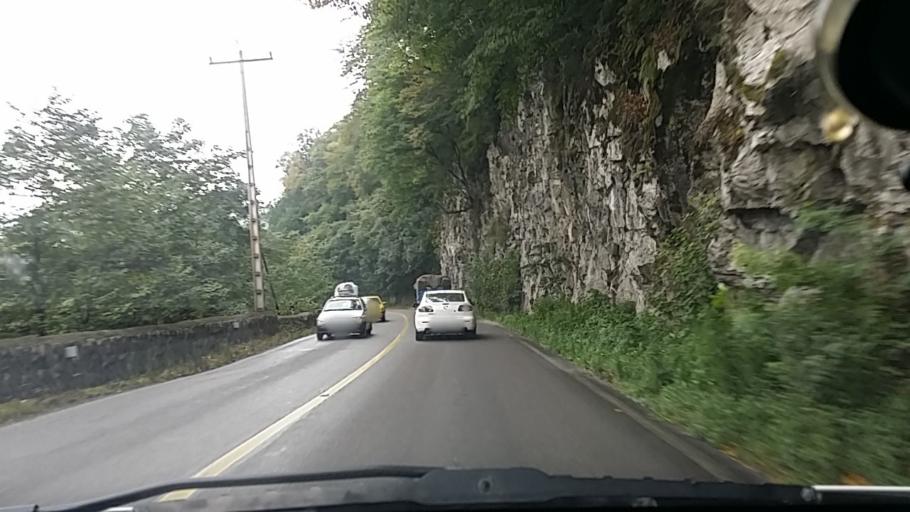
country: IR
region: Mazandaran
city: Chalus
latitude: 36.6277
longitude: 51.4017
